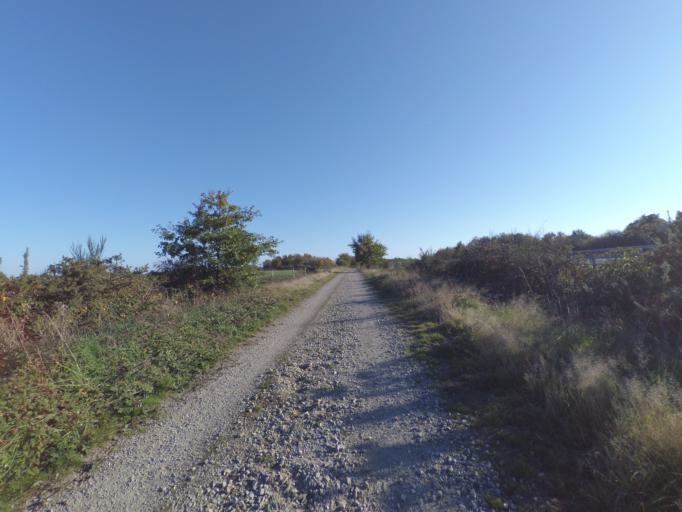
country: FR
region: Pays de la Loire
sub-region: Departement de la Loire-Atlantique
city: La Planche
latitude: 47.0234
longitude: -1.3993
